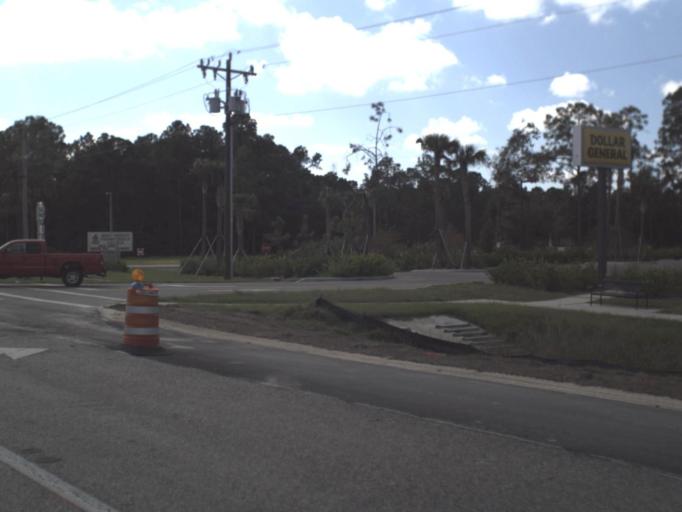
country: US
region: Florida
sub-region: Lee County
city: Suncoast Estates
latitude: 26.7436
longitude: -81.9169
